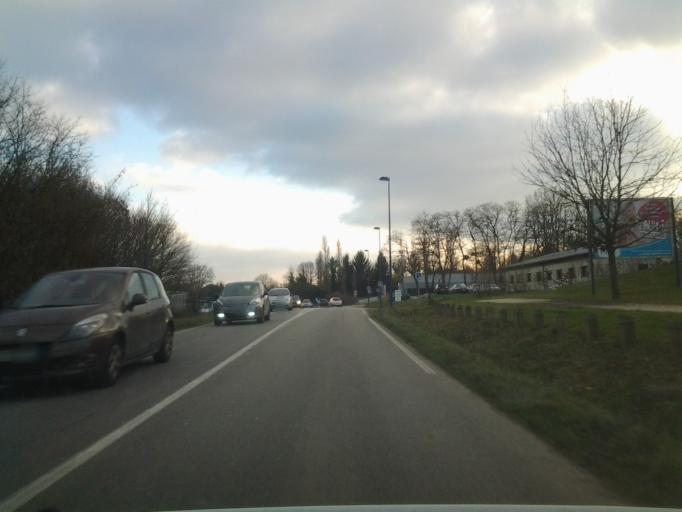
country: FR
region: Pays de la Loire
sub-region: Departement de la Vendee
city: La Roche-sur-Yon
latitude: 46.6948
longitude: -1.4246
